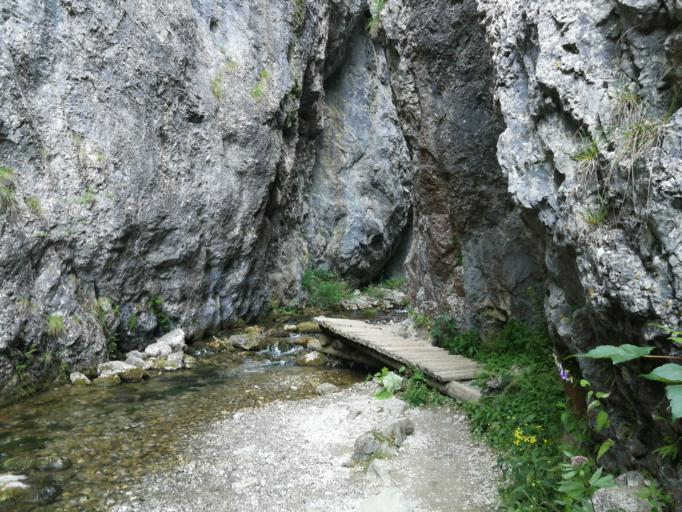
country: SK
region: Zilinsky
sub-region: Okres Liptovsky Mikulas
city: Liptovsky Mikulas
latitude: 49.1604
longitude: 19.4943
